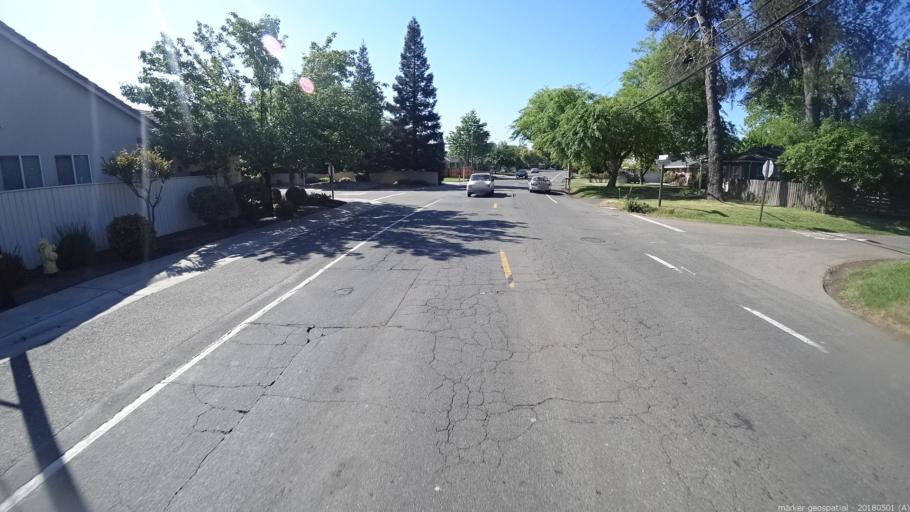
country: US
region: California
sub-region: Sacramento County
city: Arden-Arcade
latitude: 38.6357
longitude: -121.3675
